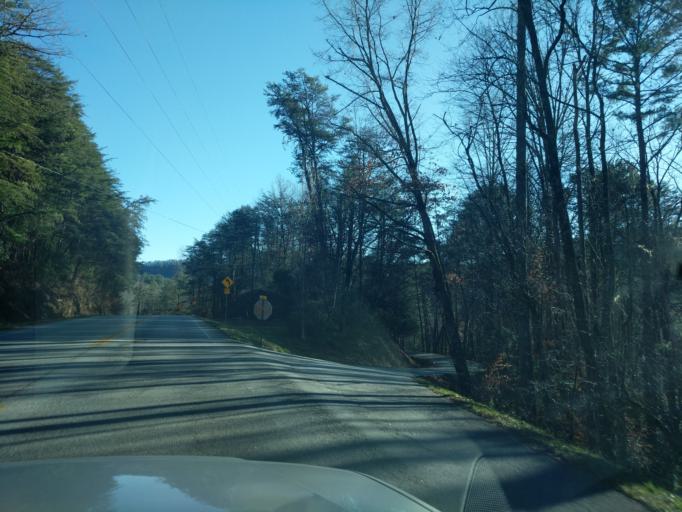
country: US
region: Georgia
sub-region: Rabun County
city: Clayton
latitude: 34.8516
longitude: -83.3629
